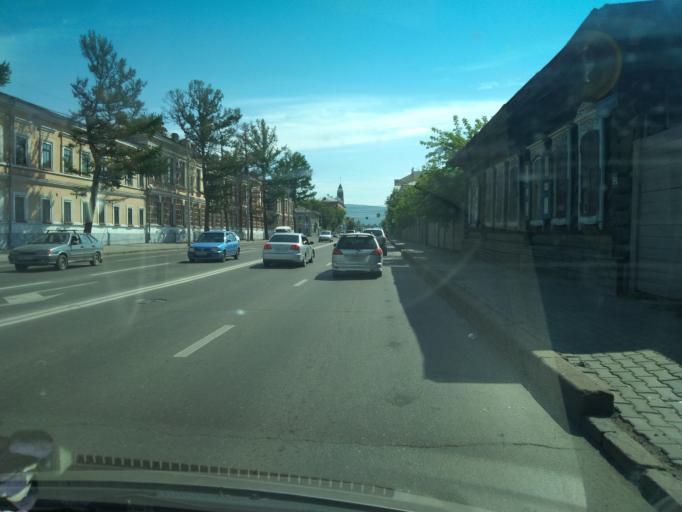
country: RU
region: Krasnoyarskiy
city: Krasnoyarsk
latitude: 56.0148
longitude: 92.8707
